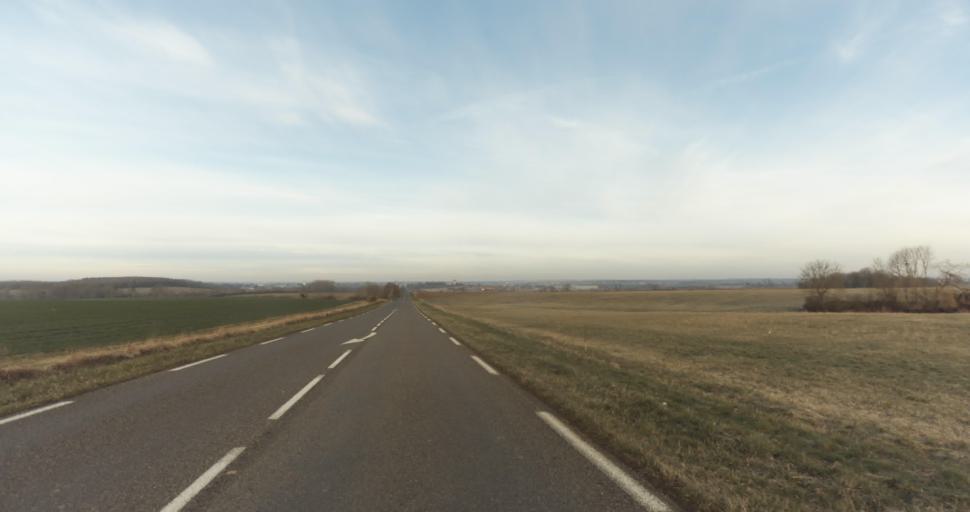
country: FR
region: Lorraine
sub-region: Departement de Meurthe-et-Moselle
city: Doncourt-les-Conflans
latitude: 49.1471
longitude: 5.9210
